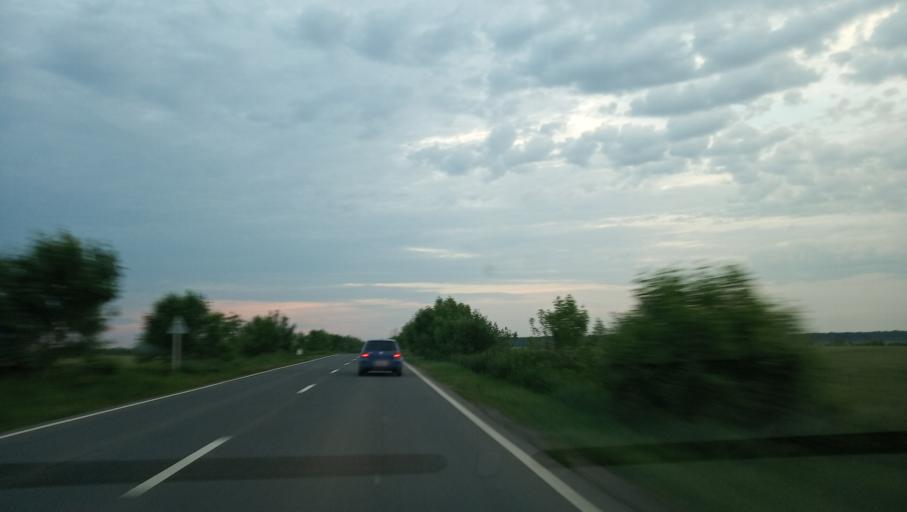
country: RO
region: Timis
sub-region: Comuna Padureni
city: Padureni
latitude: 45.6082
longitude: 21.1961
